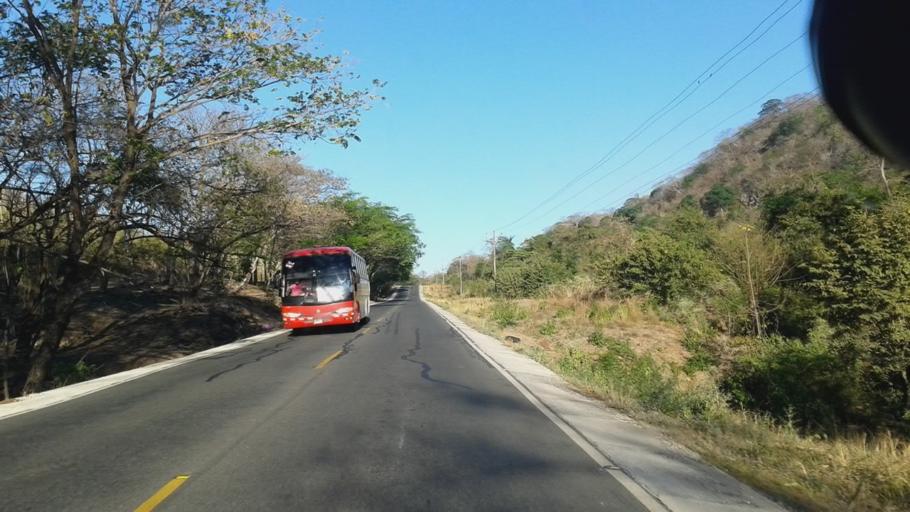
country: CR
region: Guanacaste
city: Nandayure
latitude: 10.2214
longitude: -85.2081
